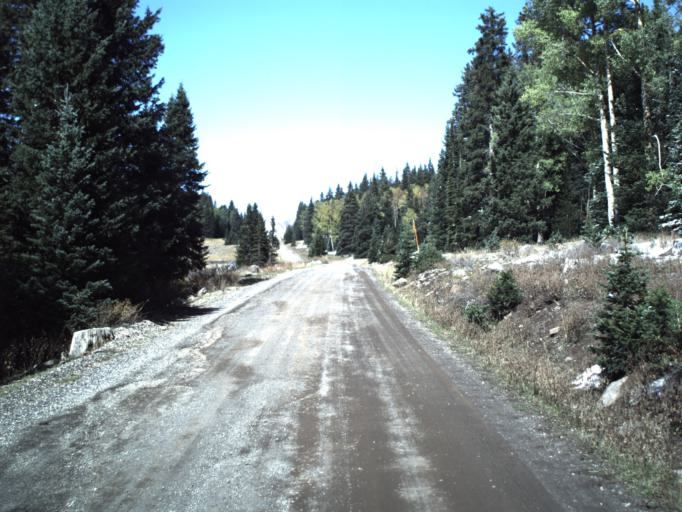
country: US
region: Utah
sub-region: Piute County
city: Junction
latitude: 38.2922
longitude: -112.3596
